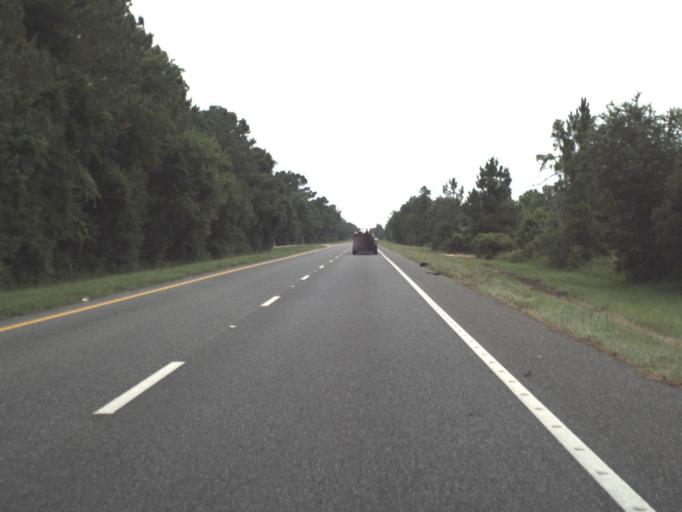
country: US
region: Florida
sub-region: Levy County
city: Bronson
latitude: 29.2868
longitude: -82.7436
